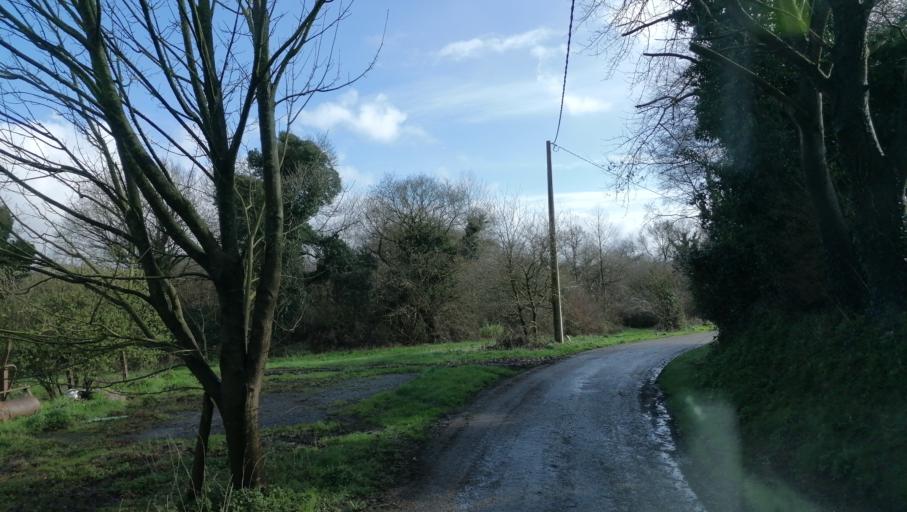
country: FR
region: Brittany
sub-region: Departement des Cotes-d'Armor
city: Lanrodec
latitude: 48.4965
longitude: -3.0202
